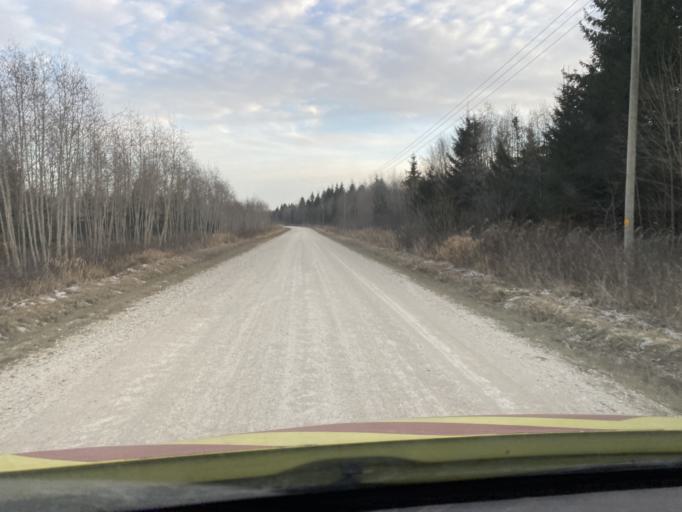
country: EE
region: Jogevamaa
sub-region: Poltsamaa linn
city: Poltsamaa
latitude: 58.5862
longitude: 26.0407
